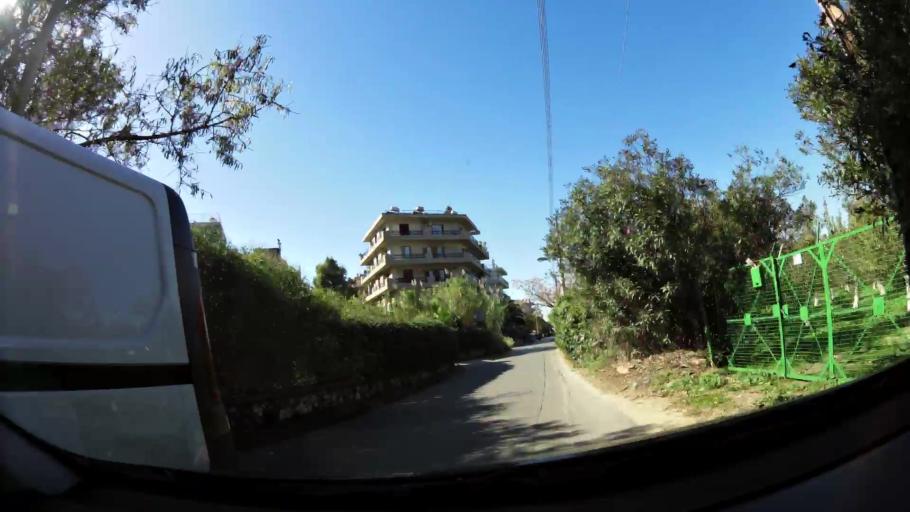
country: GR
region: Attica
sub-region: Nomarchia Athinas
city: Vrilissia
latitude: 38.0367
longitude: 23.8132
